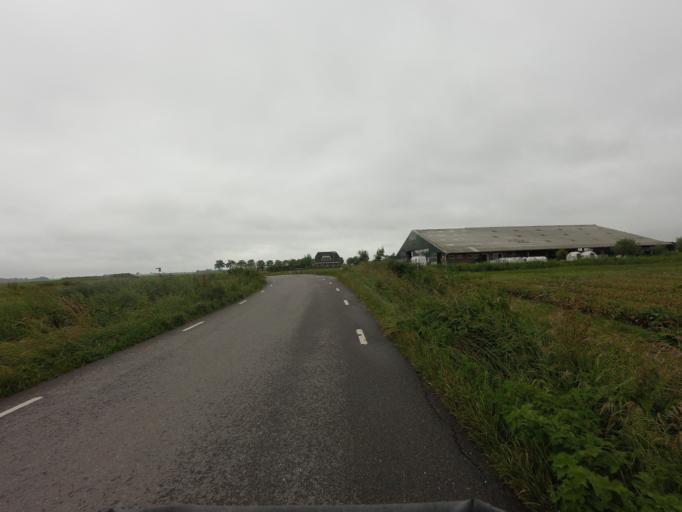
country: NL
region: North Holland
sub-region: Gemeente Schagen
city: Schagen
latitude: 52.7768
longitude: 4.8661
